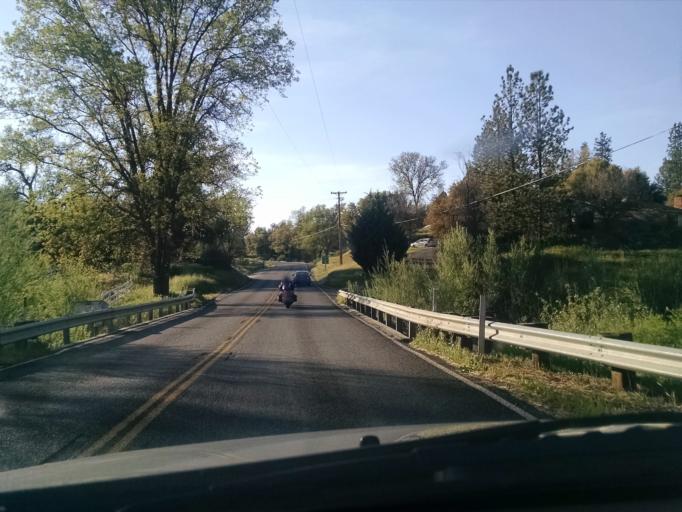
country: US
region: California
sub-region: Madera County
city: Ahwahnee
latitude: 37.3473
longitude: -119.7175
